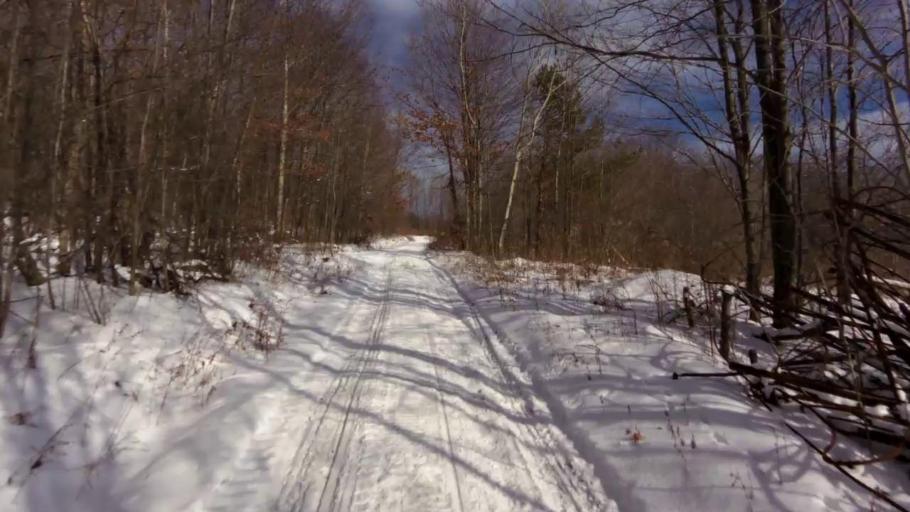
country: US
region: Pennsylvania
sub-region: McKean County
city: Foster Brook
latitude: 42.0040
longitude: -78.6155
